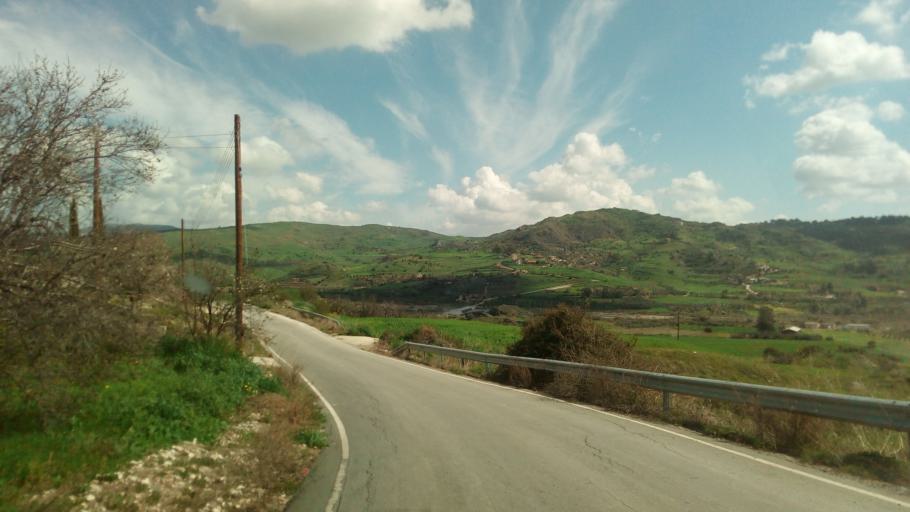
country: CY
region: Pafos
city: Mesogi
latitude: 34.7751
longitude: 32.5730
